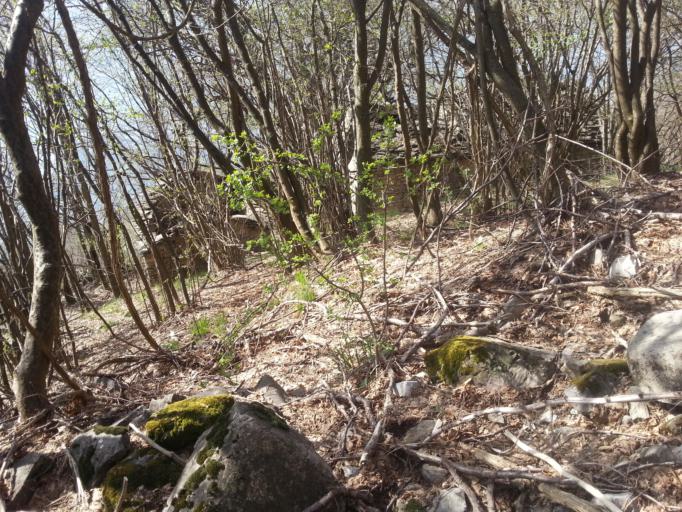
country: IT
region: Lombardy
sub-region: Provincia di Como
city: Azzano
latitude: 45.9891
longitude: 9.1918
